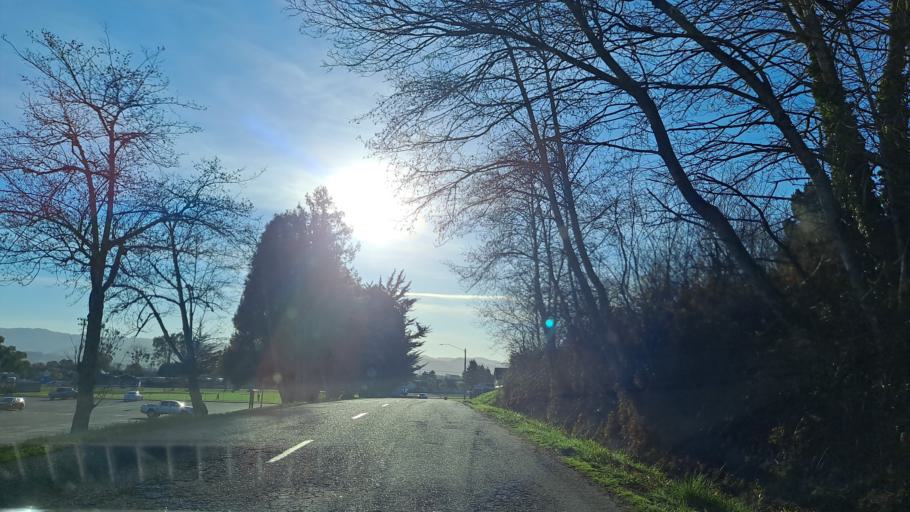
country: US
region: California
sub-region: Humboldt County
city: Fortuna
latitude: 40.5938
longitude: -124.1362
